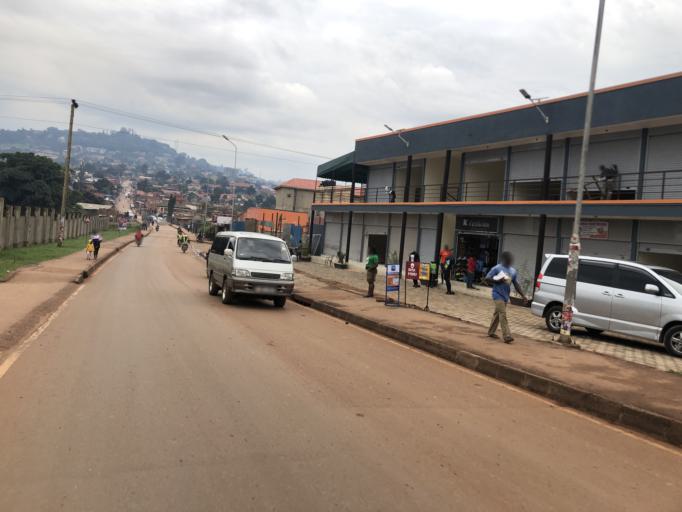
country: UG
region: Central Region
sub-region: Kampala District
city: Kampala
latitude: 0.2843
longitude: 32.6052
